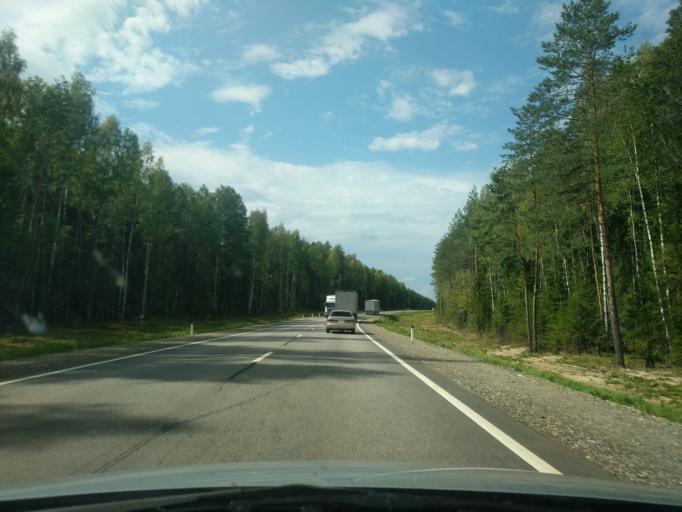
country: RU
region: Kostroma
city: Kadyy
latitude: 57.7967
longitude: 42.8456
